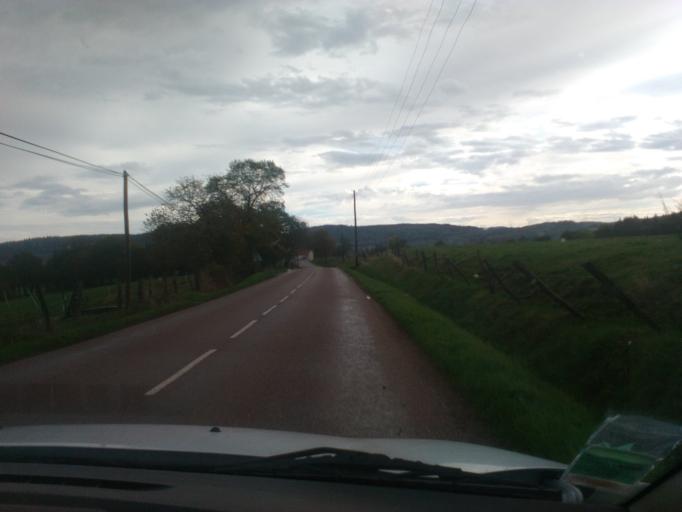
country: FR
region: Lorraine
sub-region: Departement des Vosges
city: Corcieux
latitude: 48.1736
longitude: 6.8640
